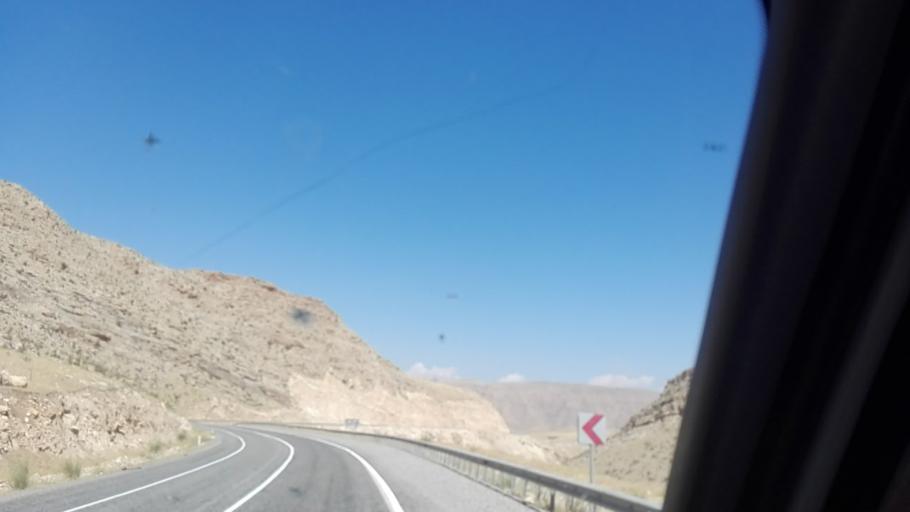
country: TR
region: Batman
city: Hasankeyf
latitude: 37.6945
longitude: 41.4588
